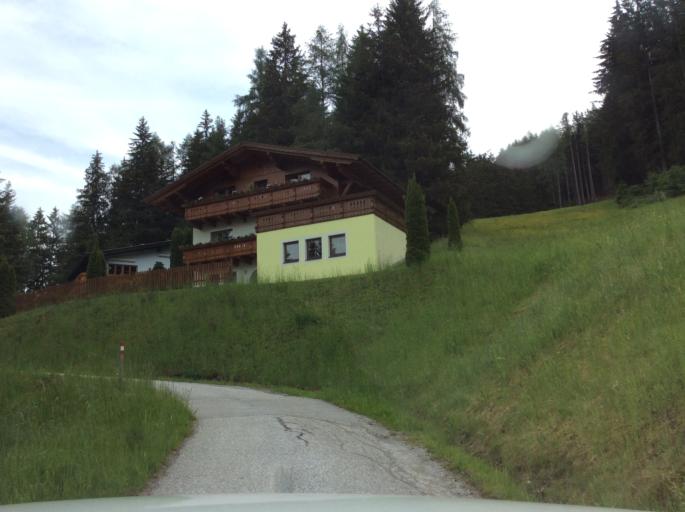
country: AT
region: Styria
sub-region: Politischer Bezirk Liezen
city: Schladming
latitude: 47.3927
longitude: 13.7031
